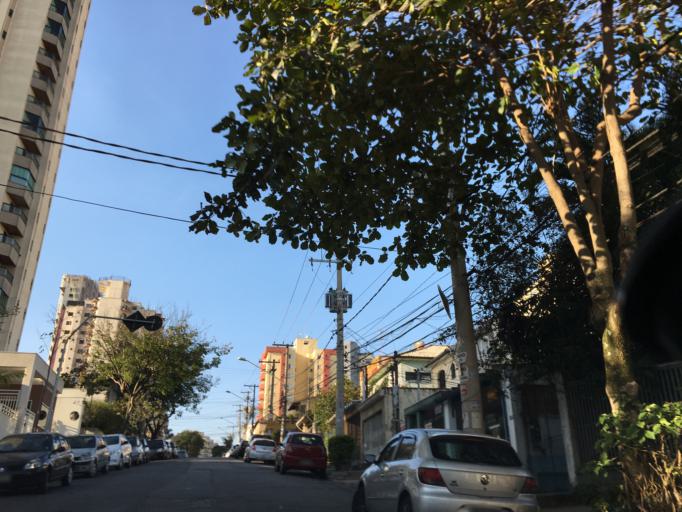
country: BR
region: Sao Paulo
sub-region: Sao Paulo
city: Sao Paulo
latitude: -23.4923
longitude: -46.6374
